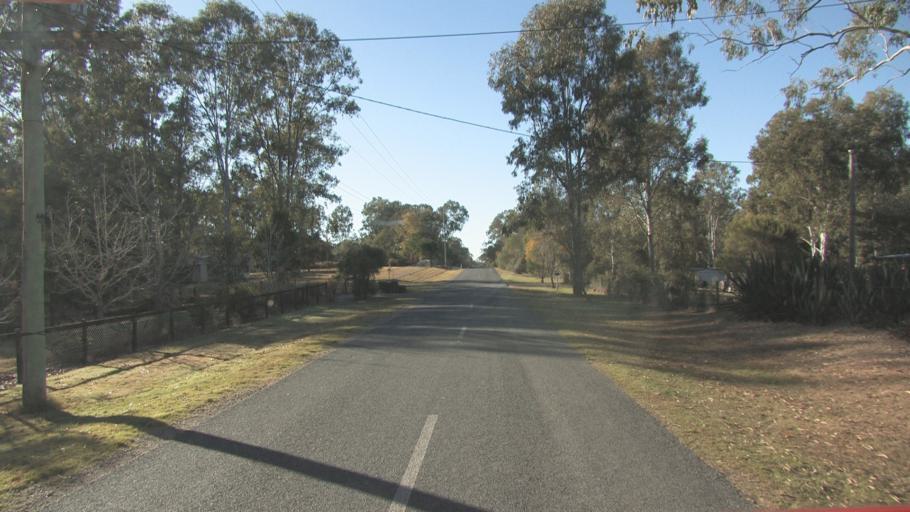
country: AU
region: Queensland
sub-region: Logan
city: North Maclean
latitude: -27.7992
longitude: 152.9977
